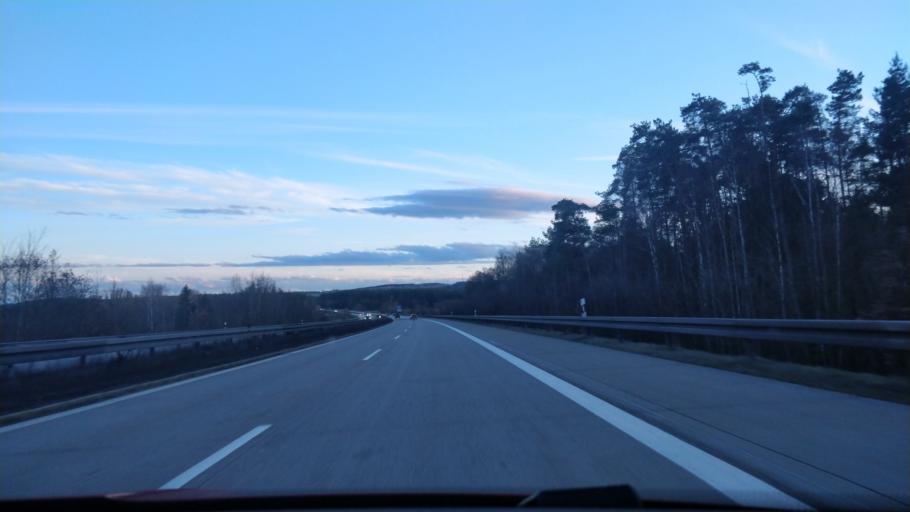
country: DE
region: Bavaria
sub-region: Upper Palatinate
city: Luhe-Wildenau
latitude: 49.5595
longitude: 12.1221
